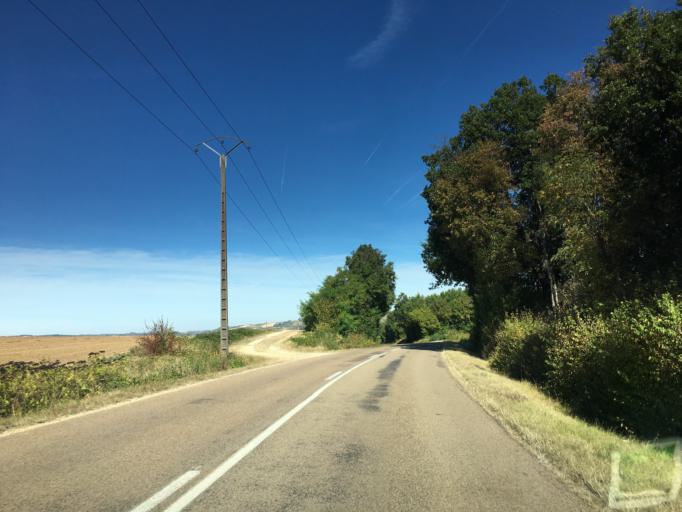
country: FR
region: Bourgogne
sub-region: Departement de l'Yonne
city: Saint-Bris-le-Vineux
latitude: 47.6831
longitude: 3.6540
